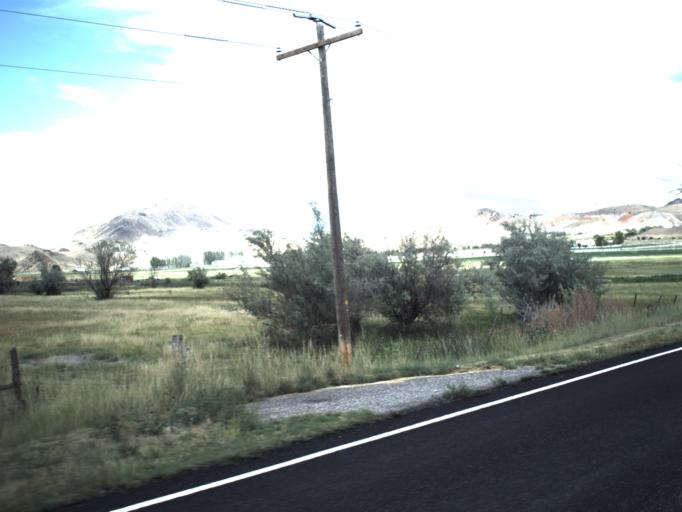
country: US
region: Utah
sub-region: Sevier County
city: Richfield
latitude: 38.7744
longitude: -111.9996
